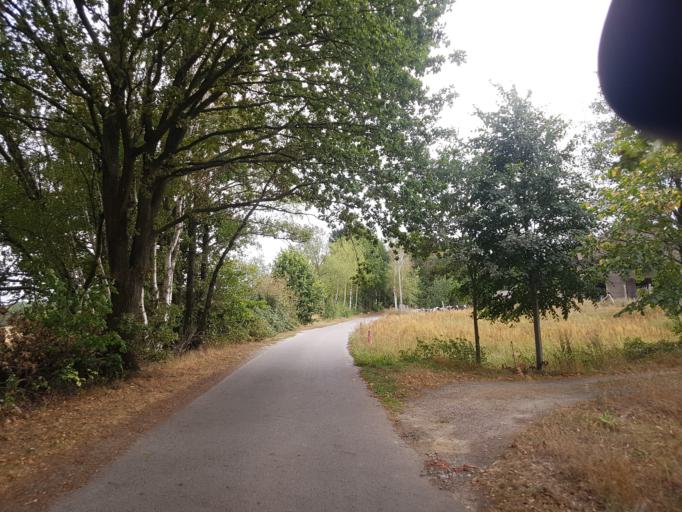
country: DE
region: Brandenburg
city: Calau
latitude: 51.7177
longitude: 13.9471
